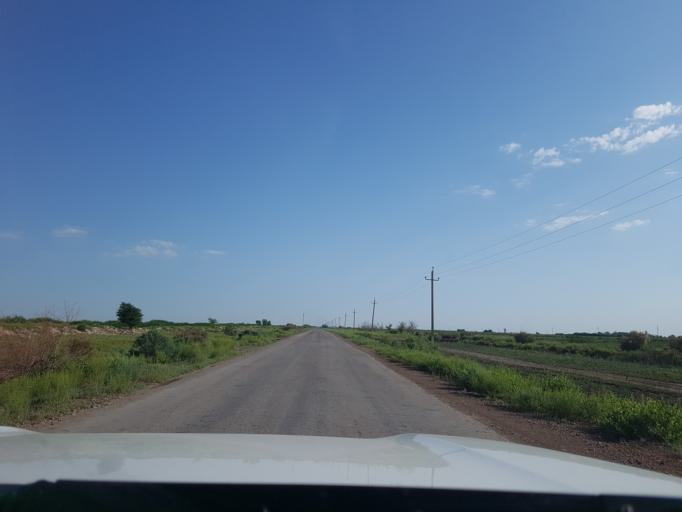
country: TM
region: Dasoguz
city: Koeneuergench
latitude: 41.8702
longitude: 58.7059
